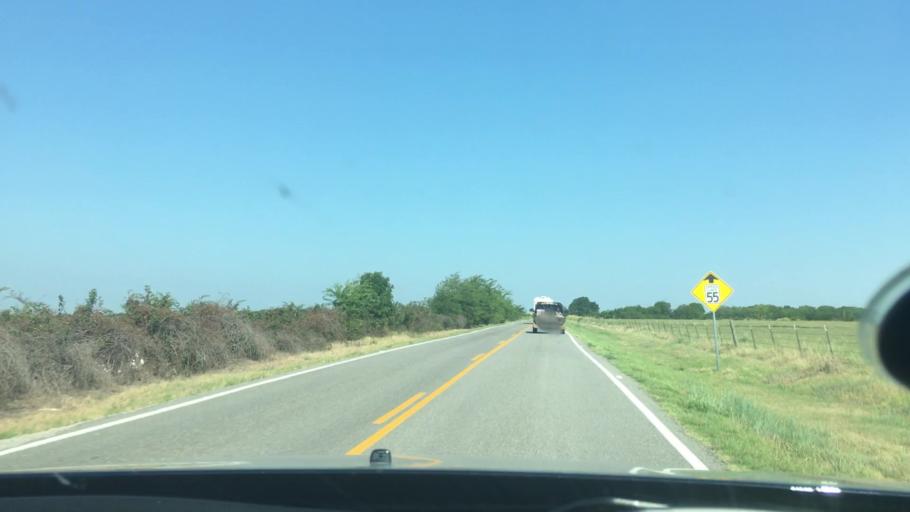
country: US
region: Oklahoma
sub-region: Johnston County
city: Tishomingo
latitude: 34.1964
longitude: -96.5391
